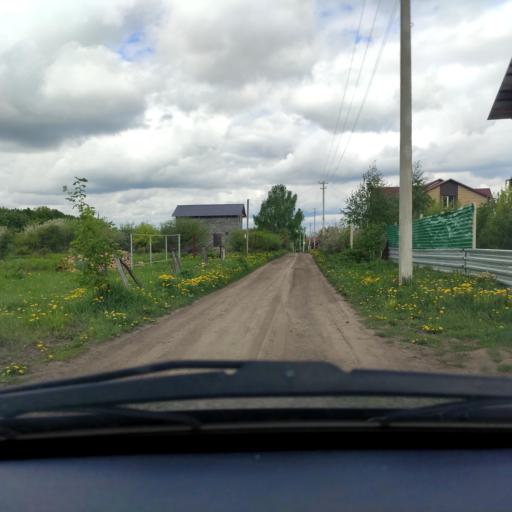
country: RU
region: Bashkortostan
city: Kabakovo
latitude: 54.7078
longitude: 56.1589
